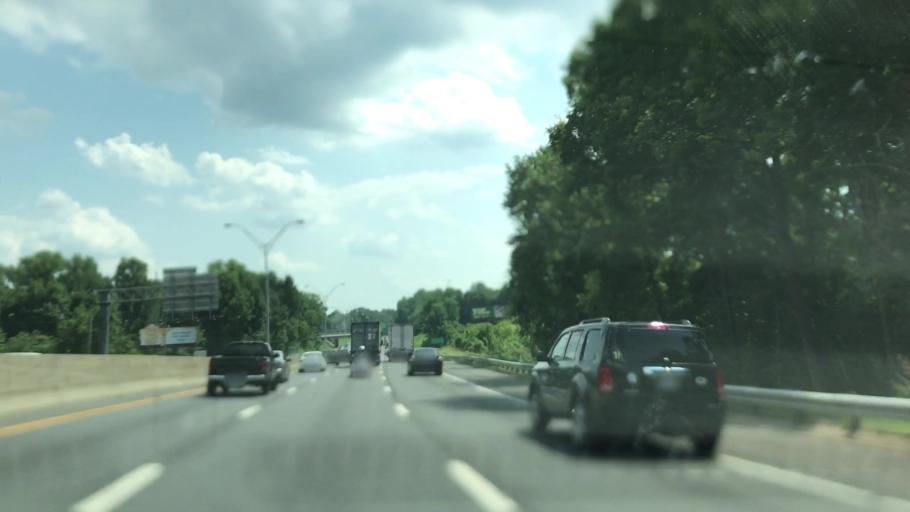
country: US
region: North Carolina
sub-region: Mecklenburg County
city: Charlotte
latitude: 35.2152
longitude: -80.8726
